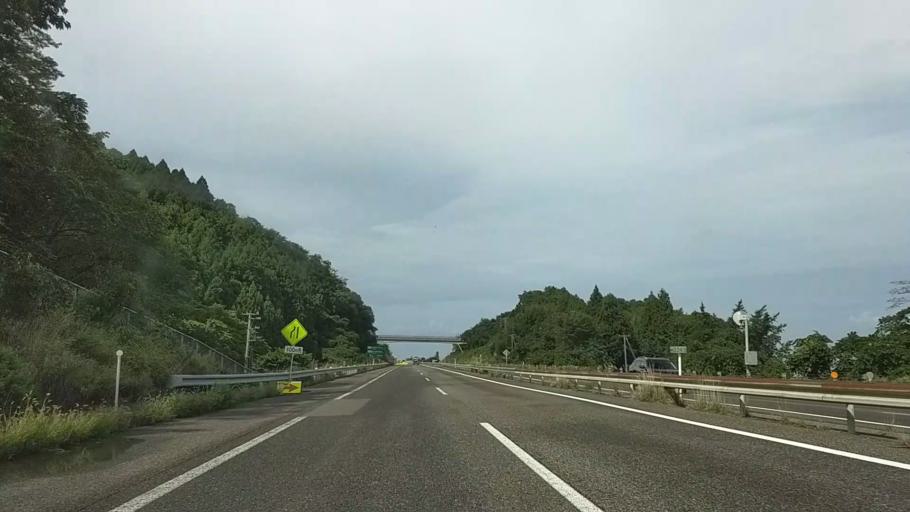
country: JP
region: Niigata
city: Itoigawa
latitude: 37.0854
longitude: 137.9645
